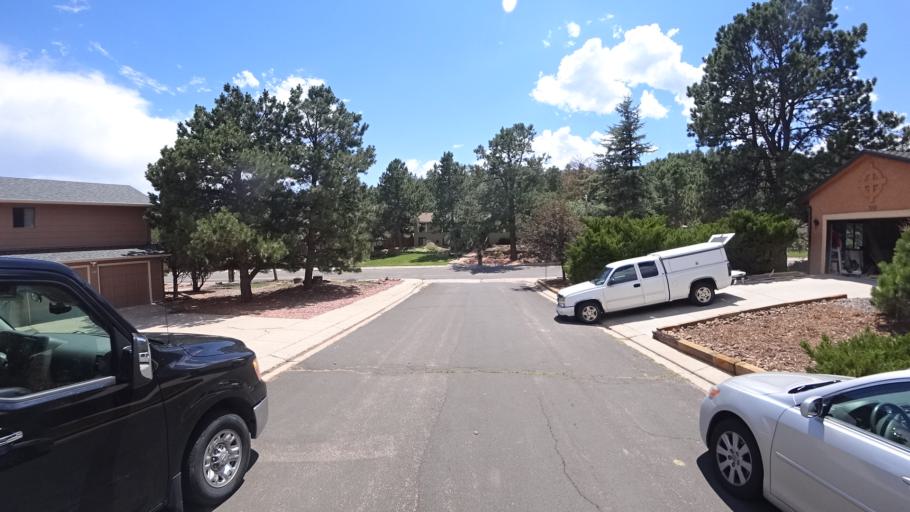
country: US
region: Colorado
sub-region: El Paso County
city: Air Force Academy
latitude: 38.9366
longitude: -104.8420
